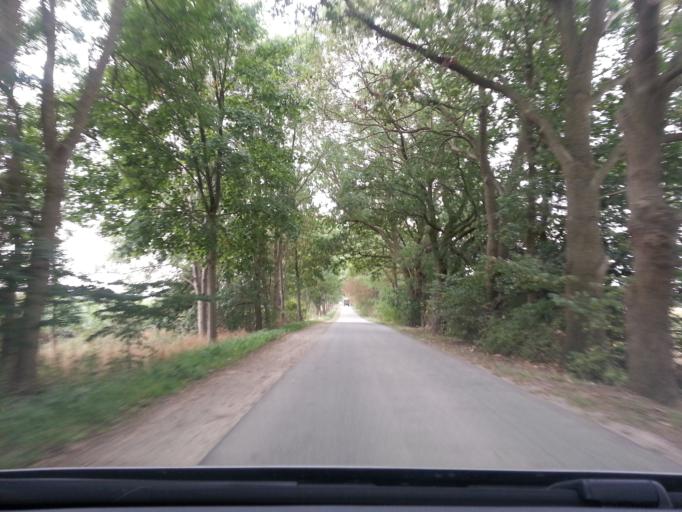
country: DE
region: Mecklenburg-Vorpommern
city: Ferdinandshof
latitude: 53.6703
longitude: 13.9162
